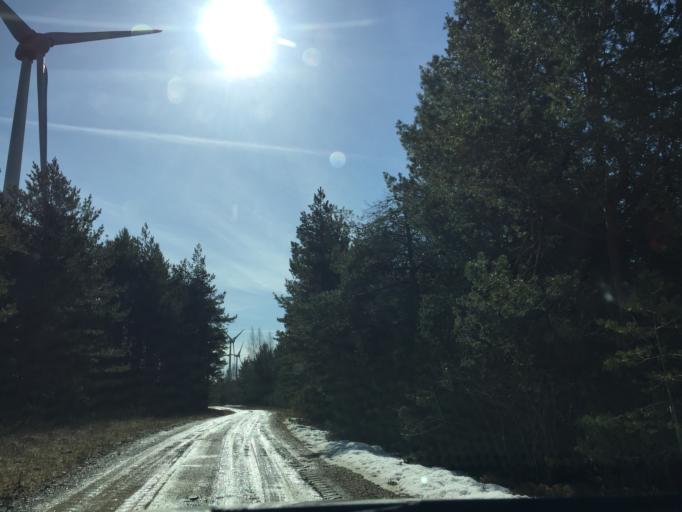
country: EE
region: Laeaene
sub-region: Haapsalu linn
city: Haapsalu
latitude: 58.6377
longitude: 23.5197
